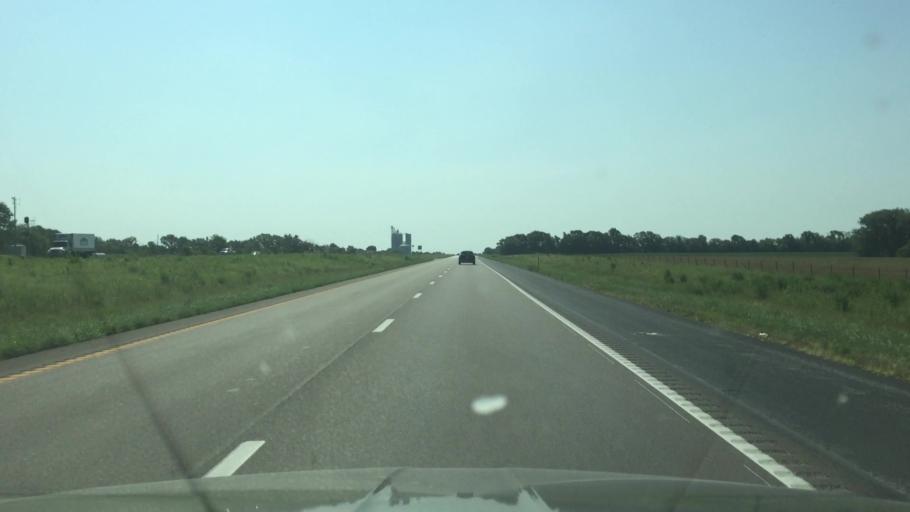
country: US
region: Missouri
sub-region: Pettis County
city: La Monte
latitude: 38.7572
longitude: -93.3662
